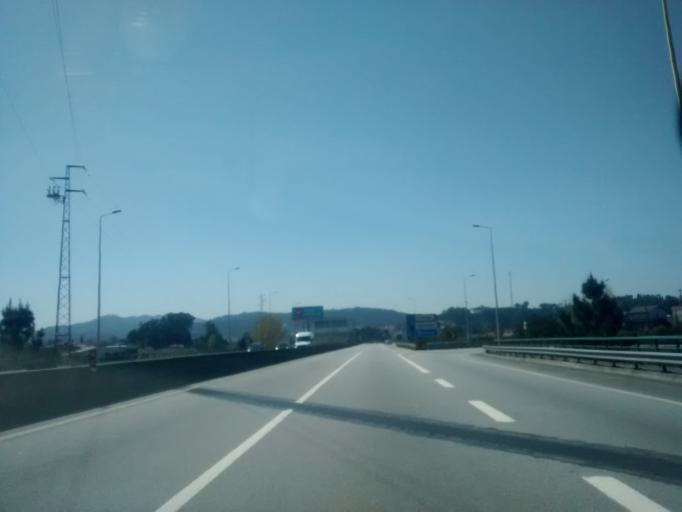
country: PT
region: Braga
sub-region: Braga
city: Braga
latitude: 41.5231
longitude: -8.4187
